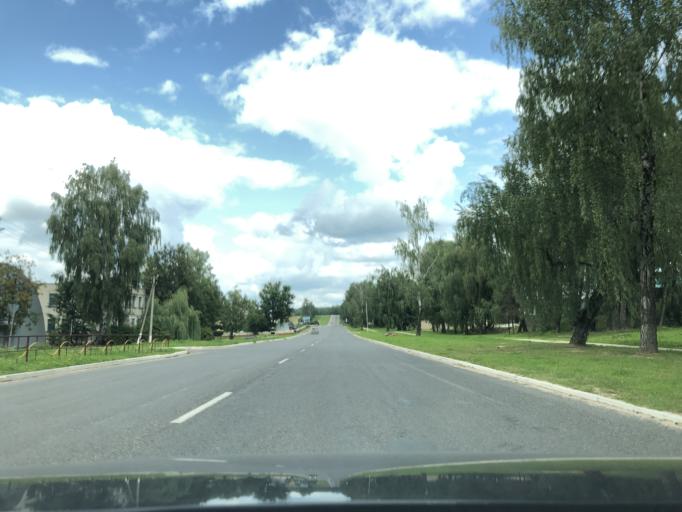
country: BY
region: Minsk
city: Lahoysk
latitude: 54.2182
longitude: 27.8513
